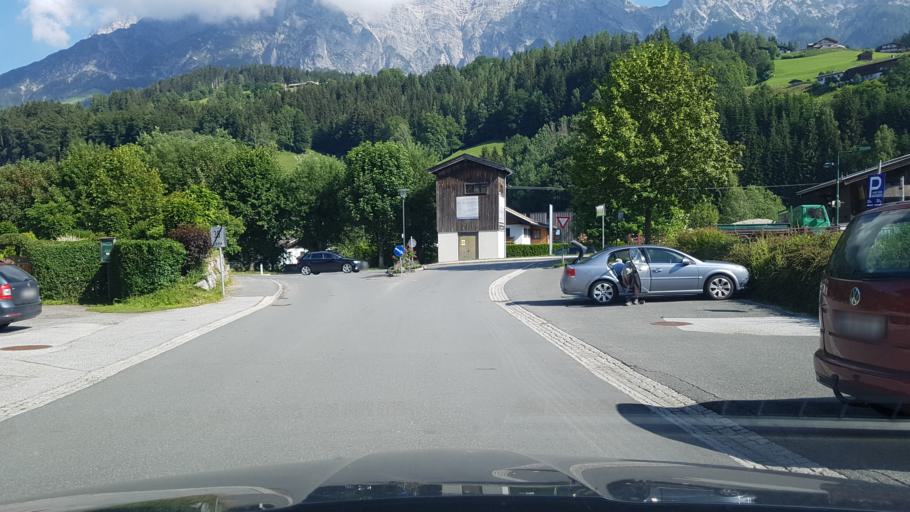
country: AT
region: Salzburg
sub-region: Politischer Bezirk Zell am See
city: Leogang
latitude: 47.4389
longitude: 12.7579
